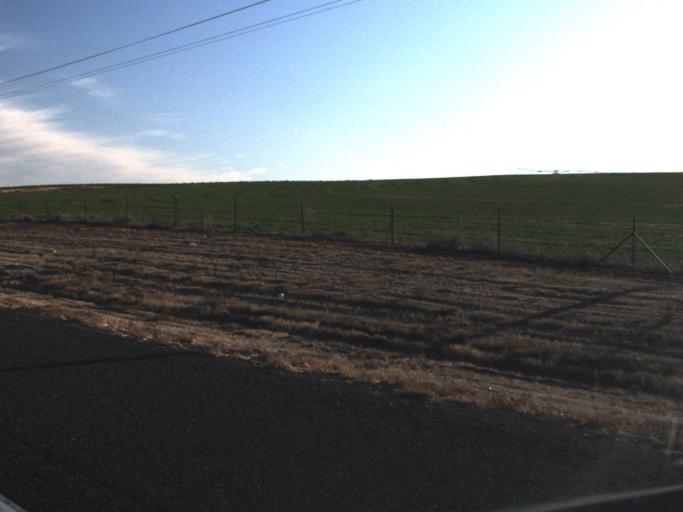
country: US
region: Washington
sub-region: Franklin County
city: Pasco
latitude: 46.3890
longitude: -119.0653
